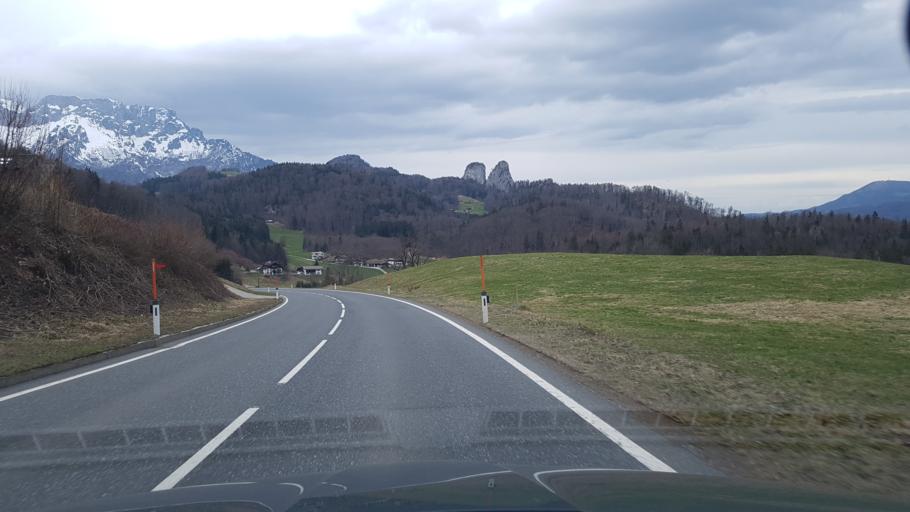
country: AT
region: Salzburg
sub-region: Politischer Bezirk Hallein
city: Hallein
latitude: 47.6707
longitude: 13.0877
